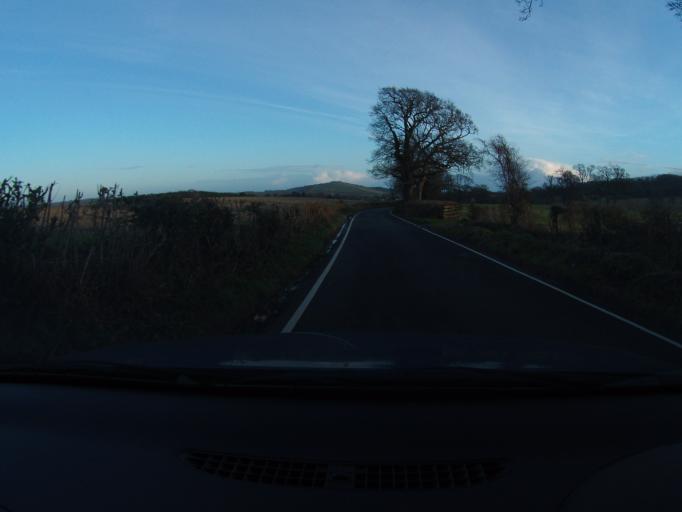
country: GB
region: England
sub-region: Isle of Wight
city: Brading
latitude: 50.6862
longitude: -1.1519
